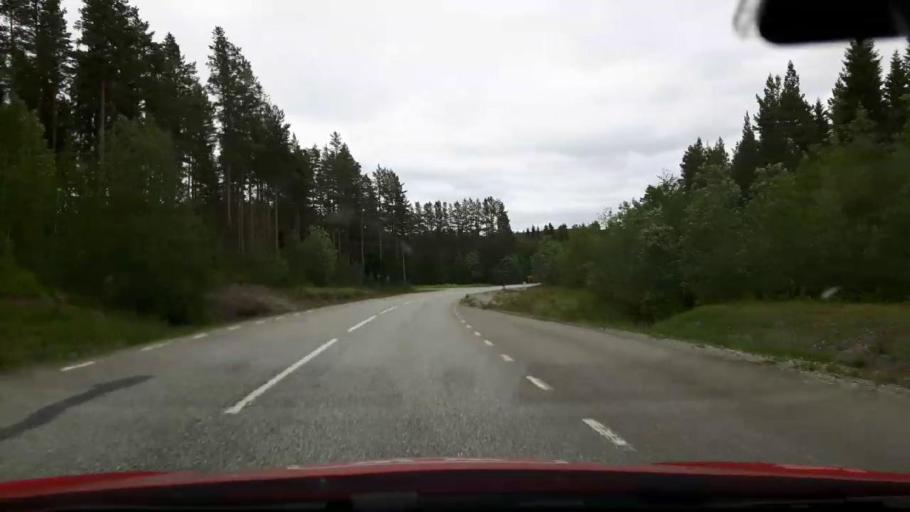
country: SE
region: Jaemtland
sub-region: Ragunda Kommun
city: Hammarstrand
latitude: 63.2616
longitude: 15.8895
